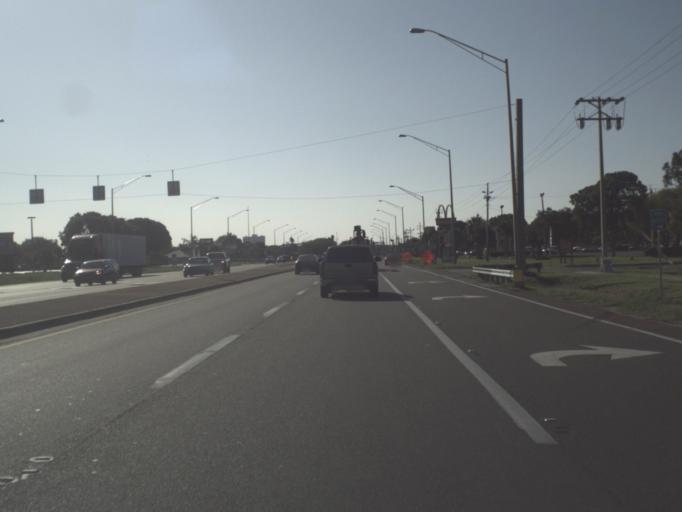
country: US
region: Florida
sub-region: Lee County
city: North Fort Myers
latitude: 26.6669
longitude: -81.8897
